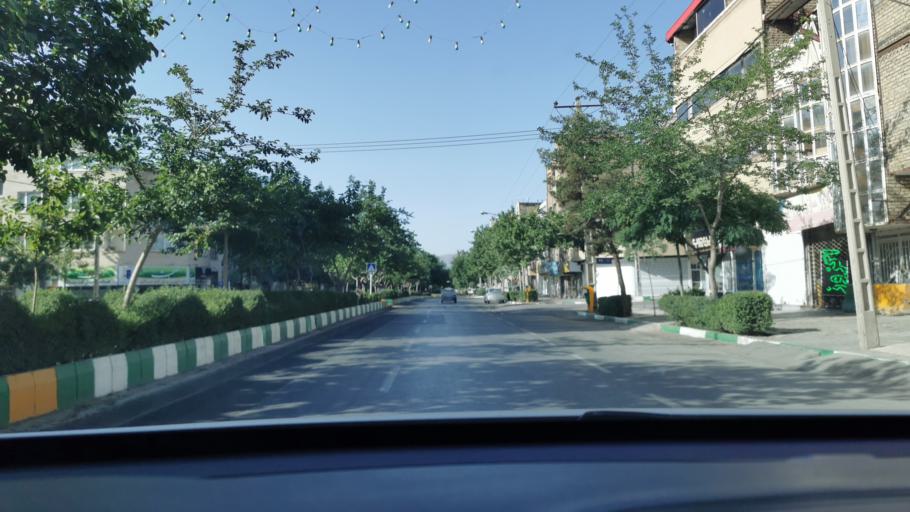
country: IR
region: Razavi Khorasan
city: Mashhad
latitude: 36.3392
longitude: 59.5135
